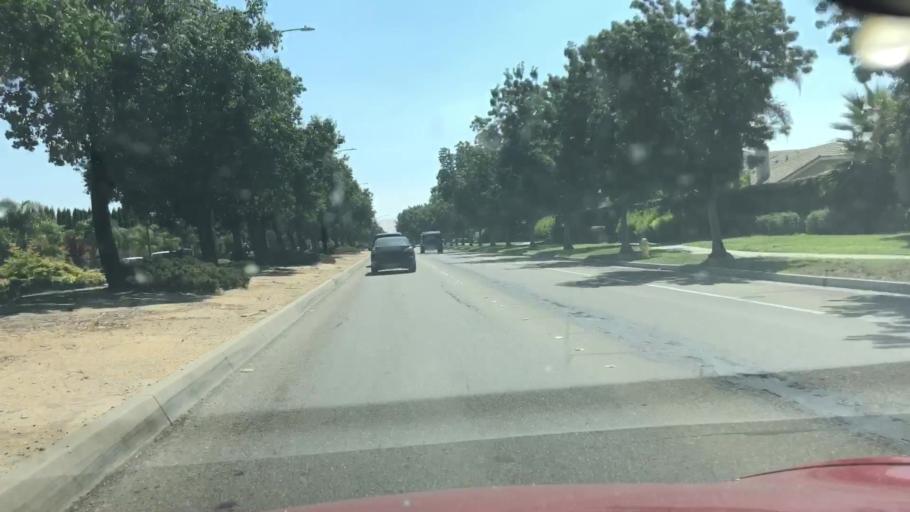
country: US
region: California
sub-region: San Joaquin County
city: Tracy
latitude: 37.7339
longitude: -121.4532
